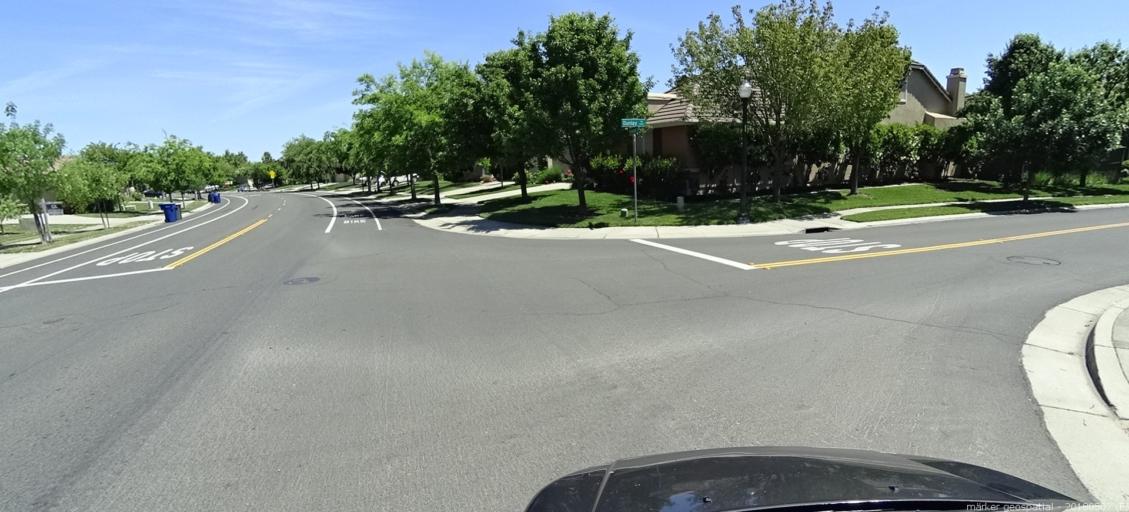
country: US
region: California
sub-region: Sacramento County
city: Elverta
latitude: 38.6803
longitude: -121.5159
